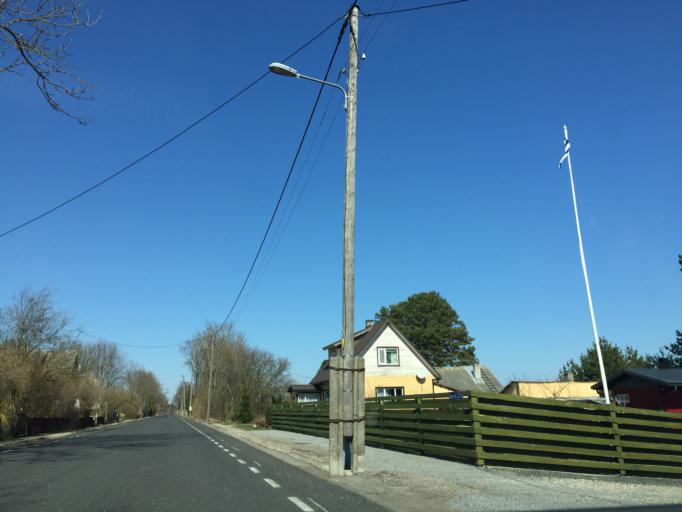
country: EE
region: Jogevamaa
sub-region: Mustvee linn
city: Mustvee
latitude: 58.8558
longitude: 26.9504
